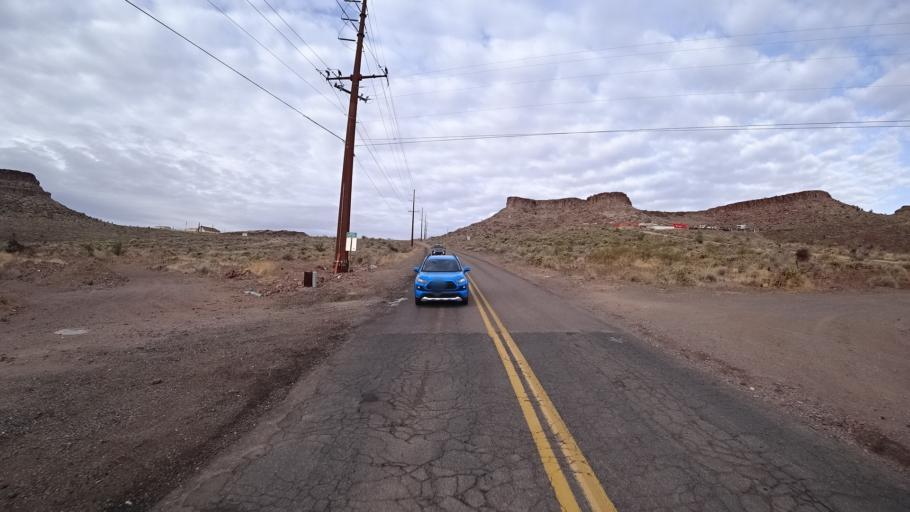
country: US
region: Arizona
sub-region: Mohave County
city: Kingman
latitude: 35.2180
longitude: -114.0583
